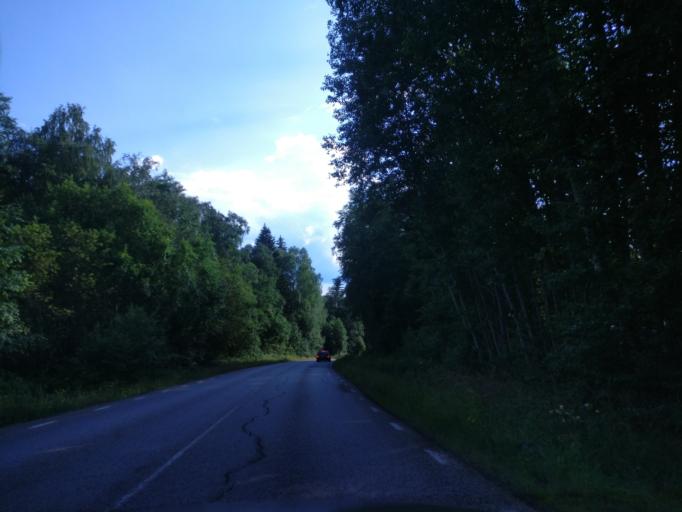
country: SE
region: Dalarna
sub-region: Ludvika Kommun
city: Ludvika
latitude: 60.2651
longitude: 15.0573
